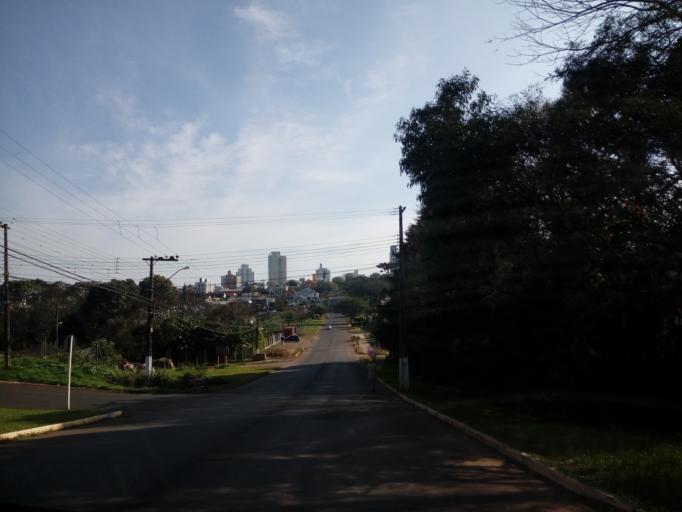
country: BR
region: Santa Catarina
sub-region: Chapeco
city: Chapeco
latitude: -27.1186
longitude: -52.6125
